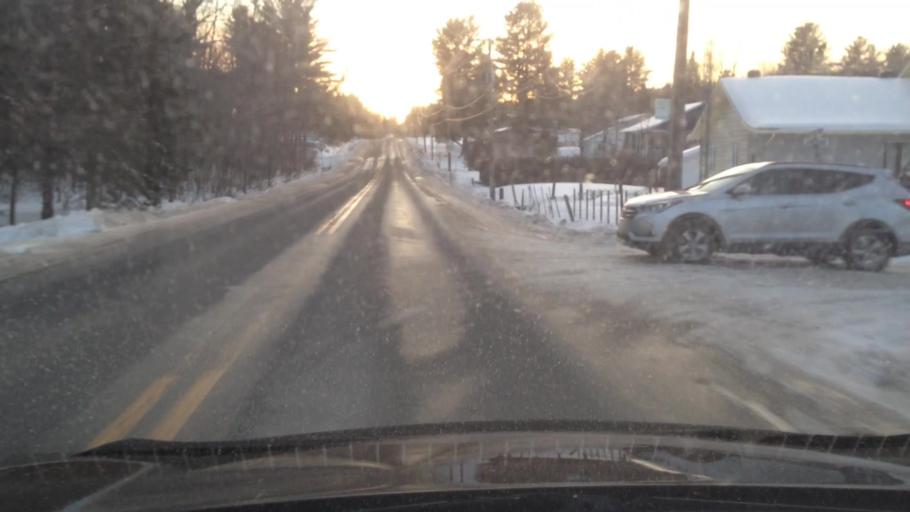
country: CA
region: Quebec
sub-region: Lanaudiere
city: Sainte-Julienne
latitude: 45.9393
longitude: -73.7307
